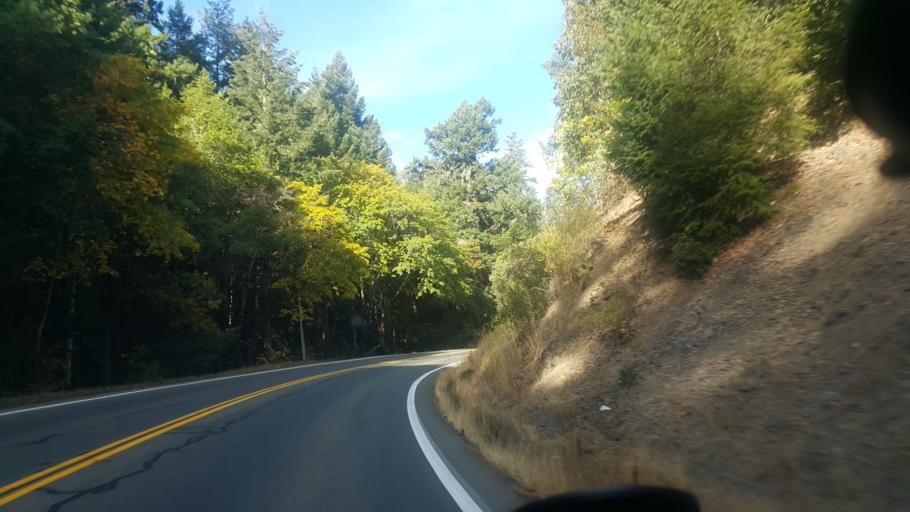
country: US
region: California
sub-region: Mendocino County
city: Brooktrails
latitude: 39.3875
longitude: -123.4359
